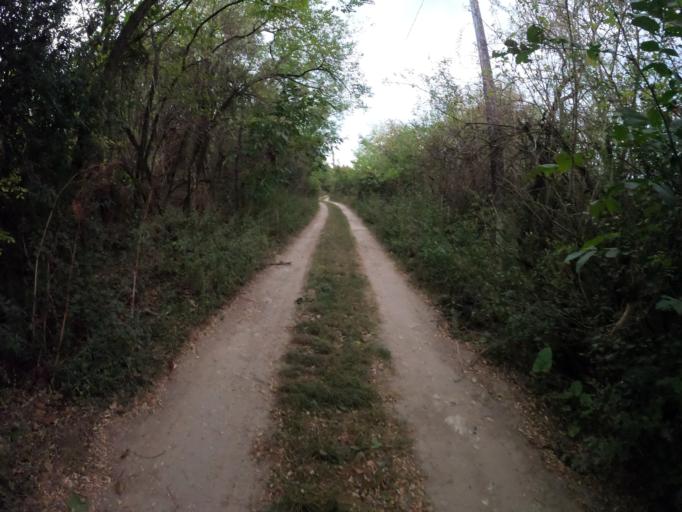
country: HU
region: Veszprem
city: Revfueloep
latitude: 46.8928
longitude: 17.5590
